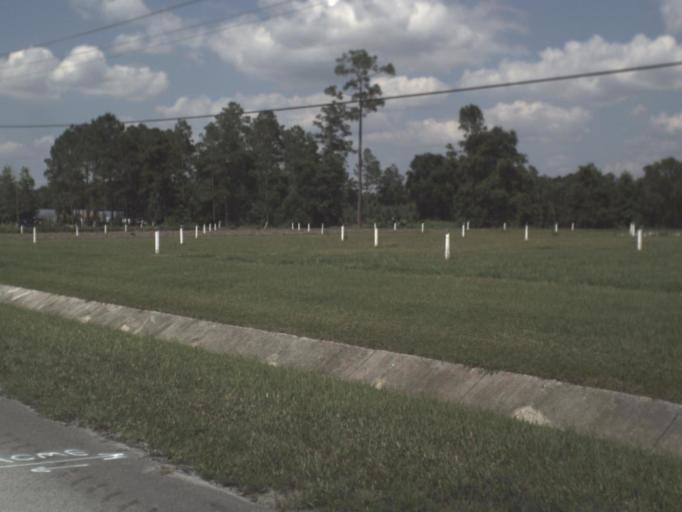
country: US
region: Florida
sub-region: Alachua County
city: Hawthorne
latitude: 29.5763
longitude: -82.0900
